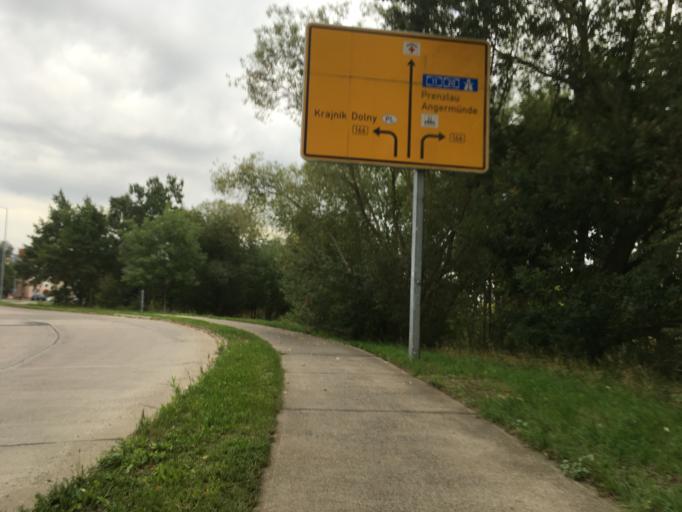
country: DE
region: Brandenburg
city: Schwedt (Oder)
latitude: 53.0657
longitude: 14.2792
